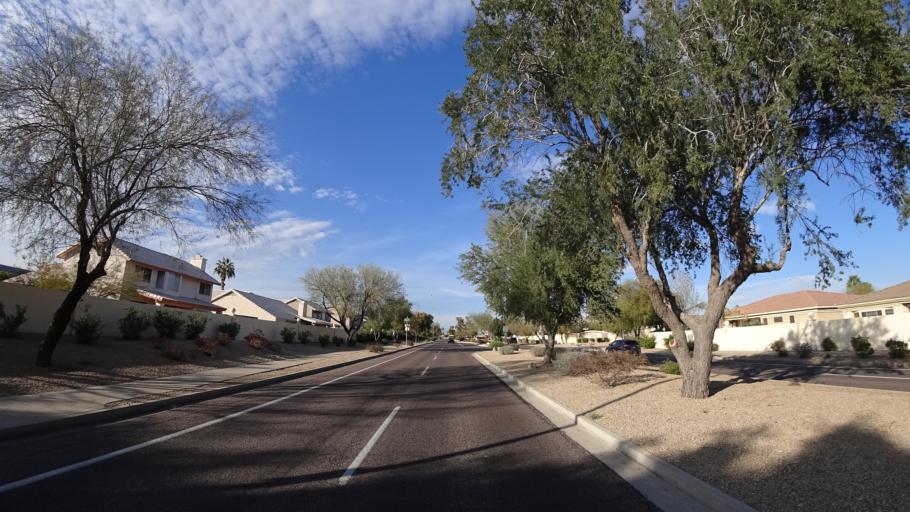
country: US
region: Arizona
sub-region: Maricopa County
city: Sun City
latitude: 33.6136
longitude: -112.2536
